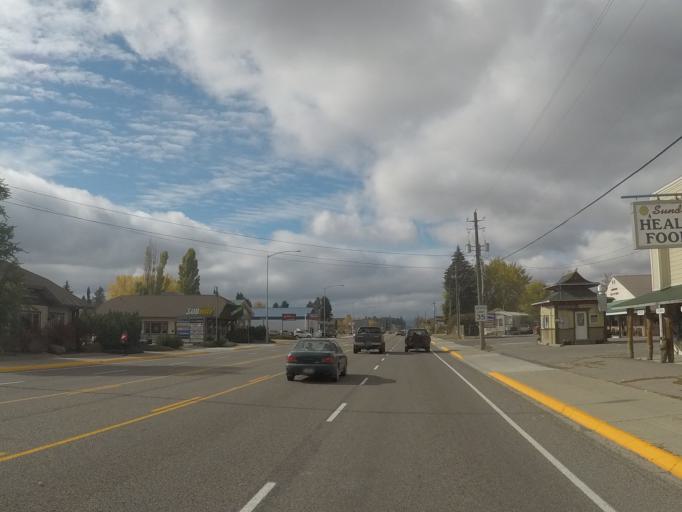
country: US
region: Montana
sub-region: Flathead County
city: Columbia Falls
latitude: 48.3707
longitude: -114.1906
